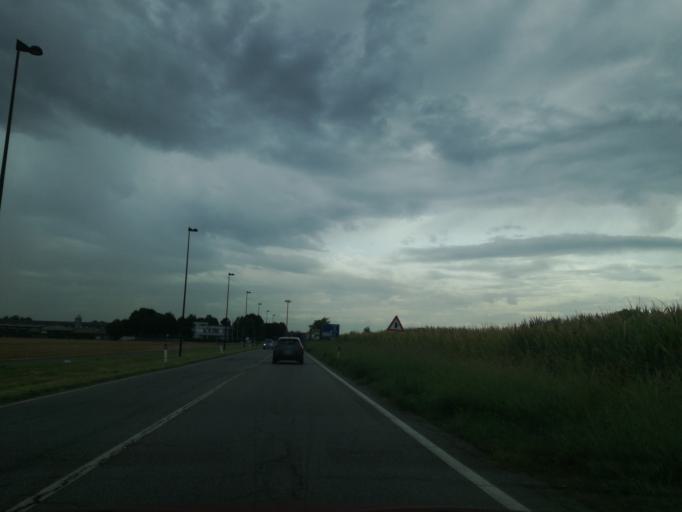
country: IT
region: Lombardy
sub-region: Provincia di Monza e Brianza
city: Bellusco
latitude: 45.6097
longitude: 9.4192
